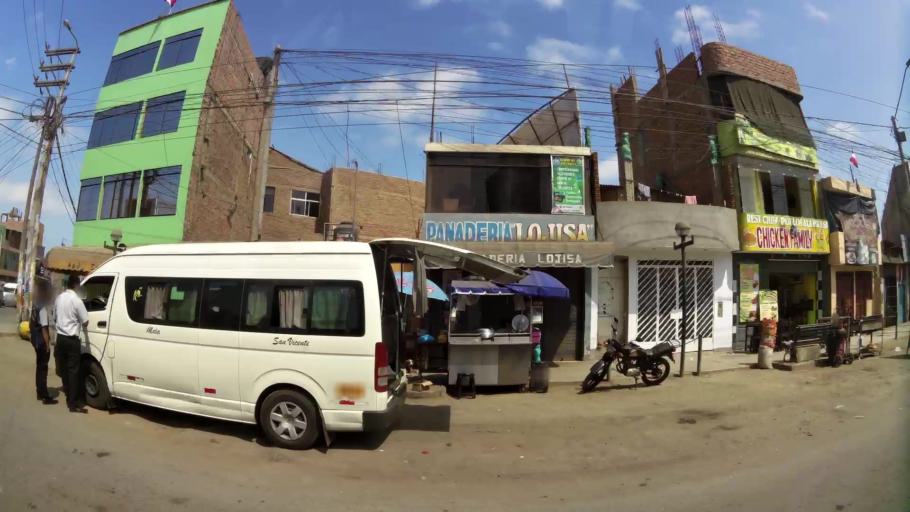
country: PE
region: Lima
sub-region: Provincia de Canete
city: Mala
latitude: -12.6561
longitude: -76.6365
